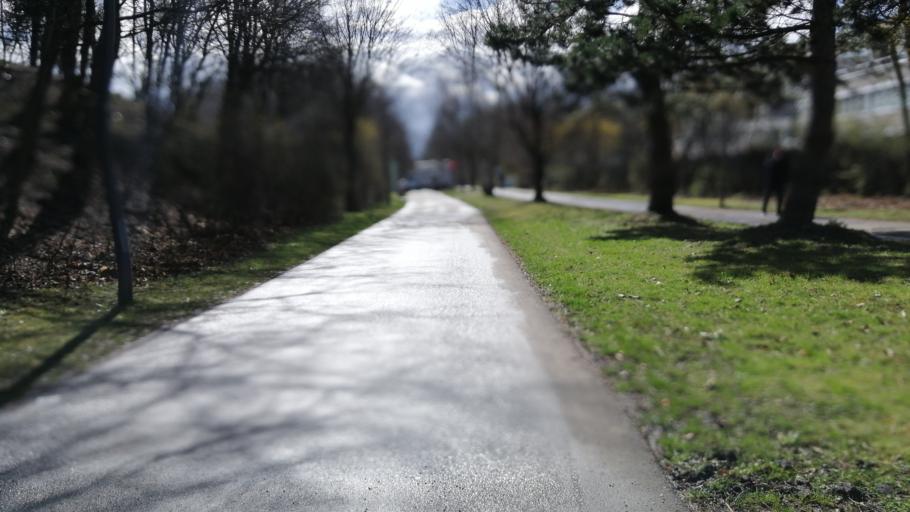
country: DE
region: Bavaria
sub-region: Upper Bavaria
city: Munich
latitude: 48.1932
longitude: 11.5755
